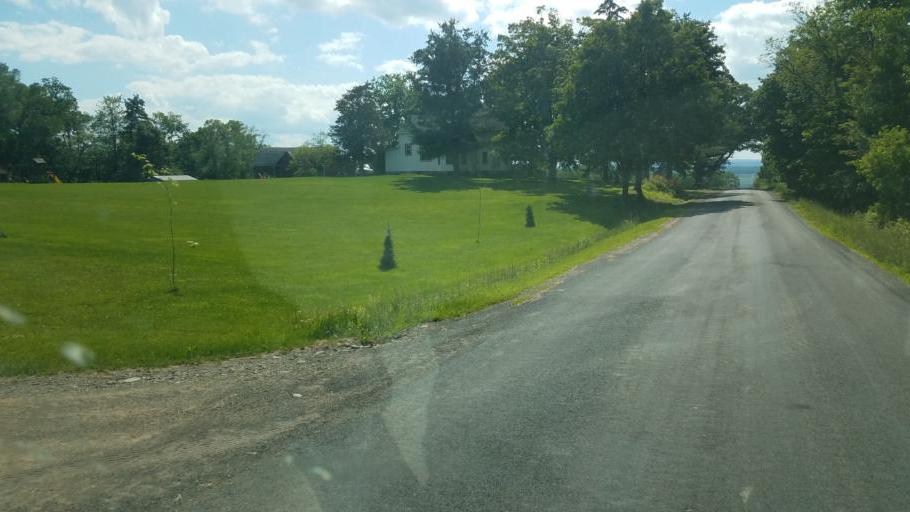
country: US
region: New York
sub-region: Yates County
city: Keuka Park
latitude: 42.5588
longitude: -77.0609
